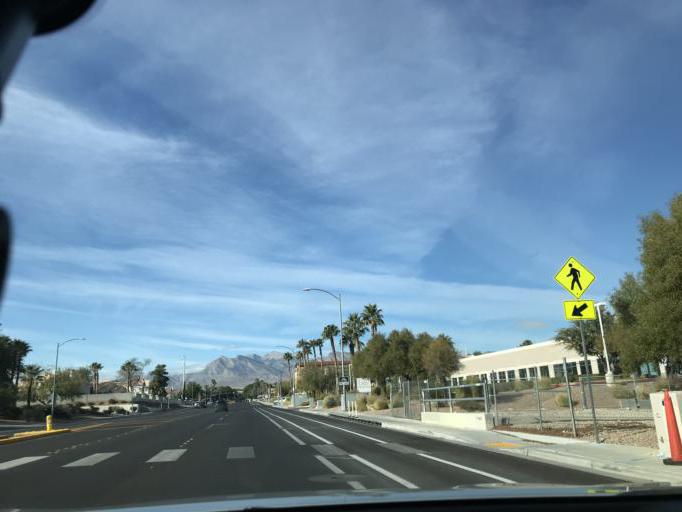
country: US
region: Nevada
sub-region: Clark County
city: Spring Valley
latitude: 36.2035
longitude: -115.2556
